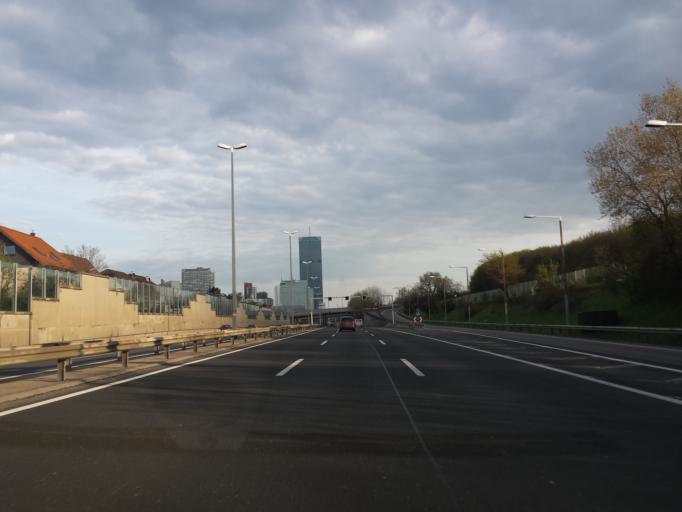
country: AT
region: Vienna
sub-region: Wien Stadt
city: Vienna
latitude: 48.2436
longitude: 16.3981
